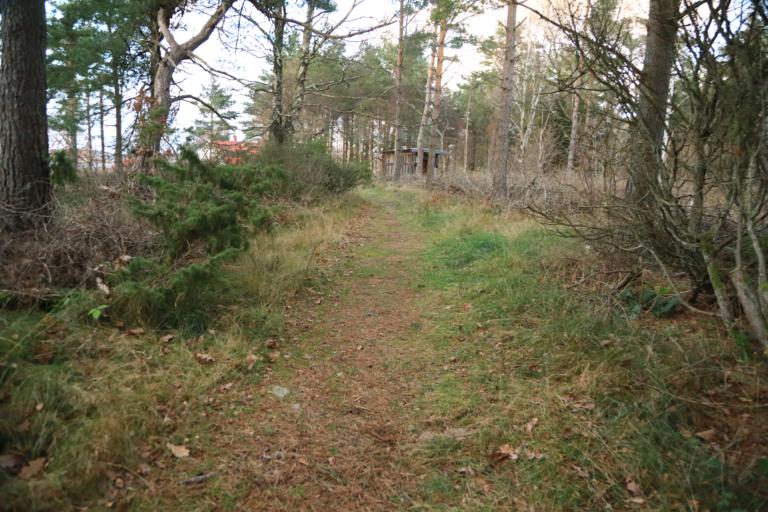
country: SE
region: Halland
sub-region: Varbergs Kommun
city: Varberg
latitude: 57.1475
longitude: 12.2212
